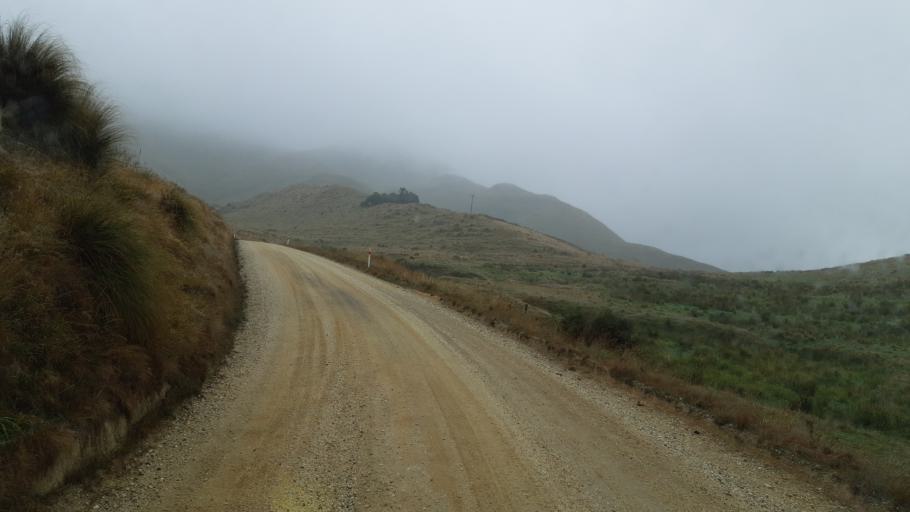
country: NZ
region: Otago
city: Oamaru
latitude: -44.9693
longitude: 170.4850
